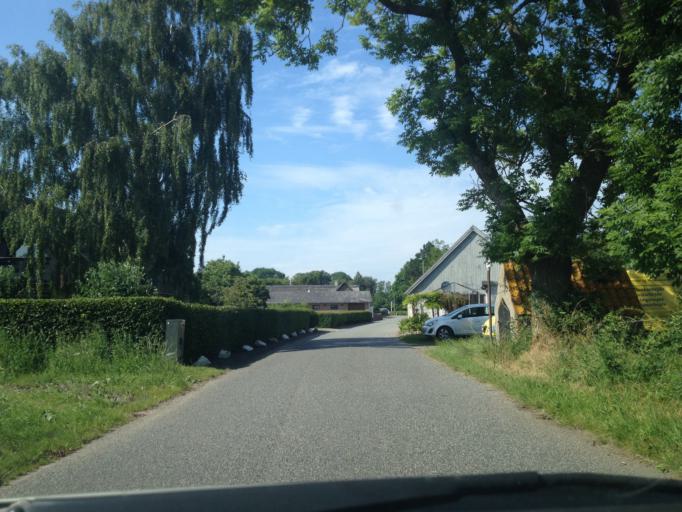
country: DK
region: Central Jutland
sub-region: Samso Kommune
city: Tranebjerg
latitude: 55.8101
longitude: 10.5560
